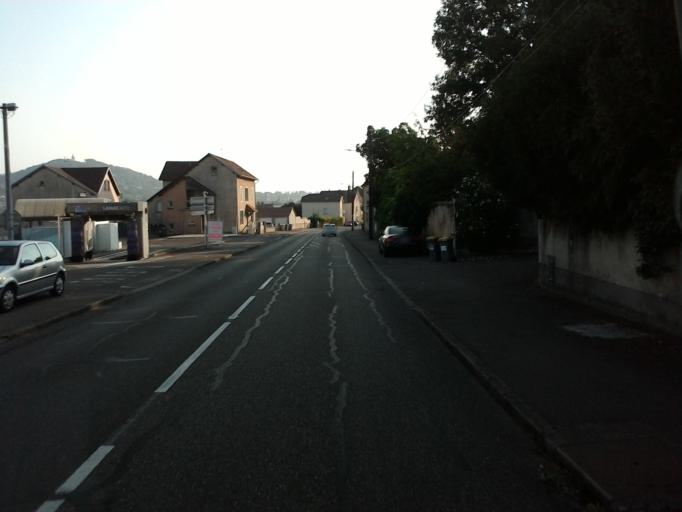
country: FR
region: Franche-Comte
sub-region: Departement de la Haute-Saone
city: Navenne
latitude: 47.6112
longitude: 6.1473
